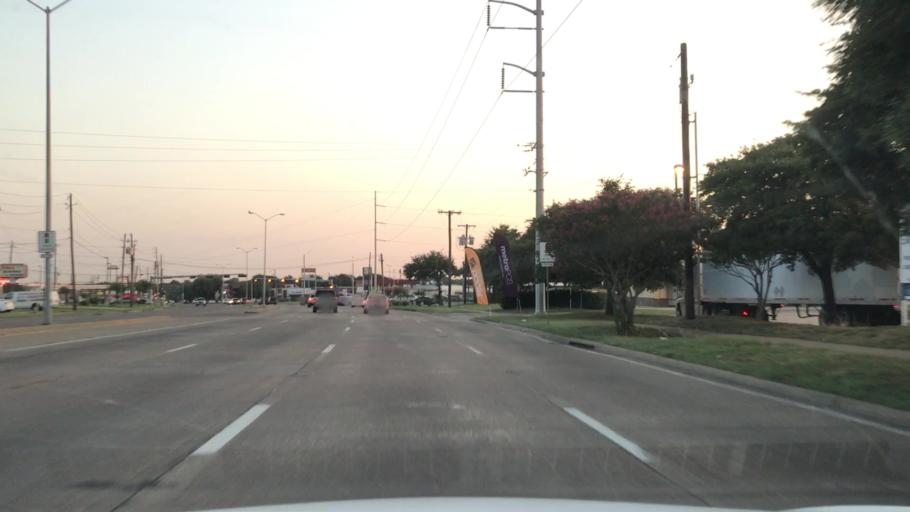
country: US
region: Texas
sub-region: Dallas County
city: Mesquite
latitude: 32.8051
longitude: -96.6824
